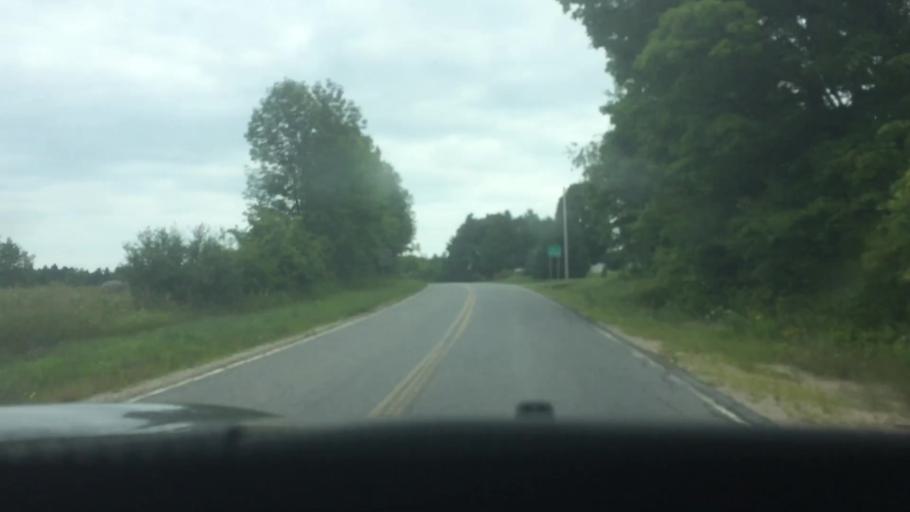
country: US
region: New York
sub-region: St. Lawrence County
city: Hannawa Falls
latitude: 44.5739
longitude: -74.9044
